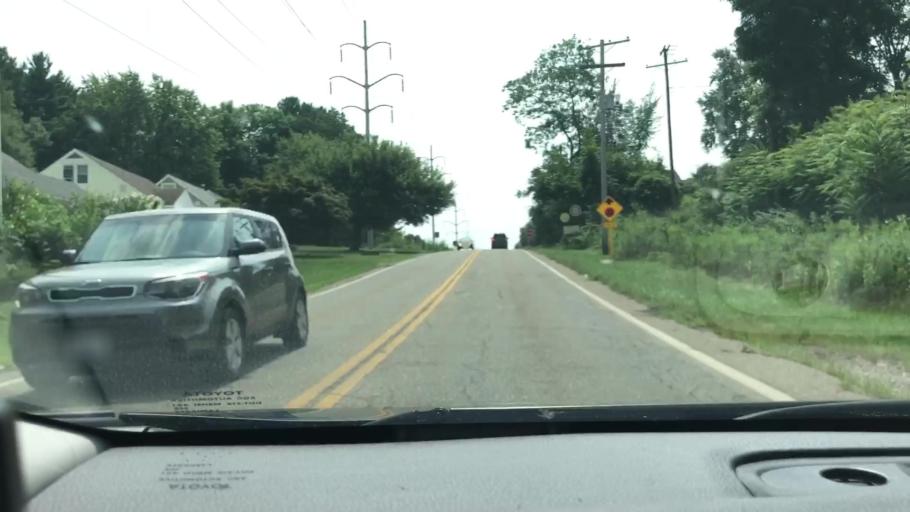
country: US
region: Ohio
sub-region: Stark County
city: Perry Heights
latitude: 40.8183
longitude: -81.4348
